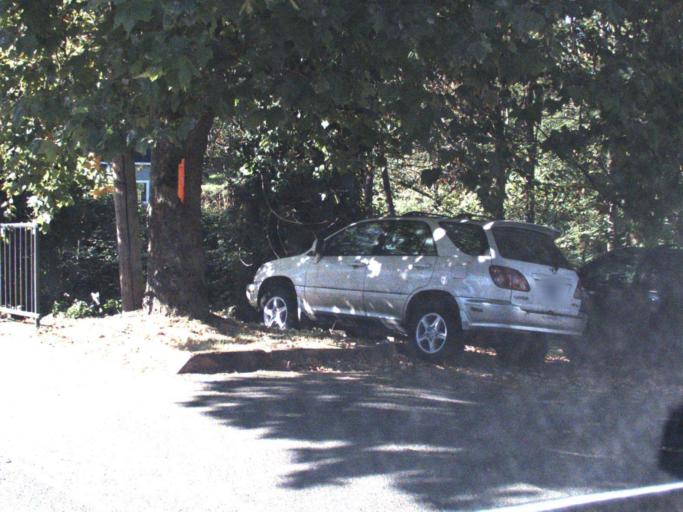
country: US
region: Washington
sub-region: King County
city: East Hill-Meridian
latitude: 47.4289
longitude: -122.1971
